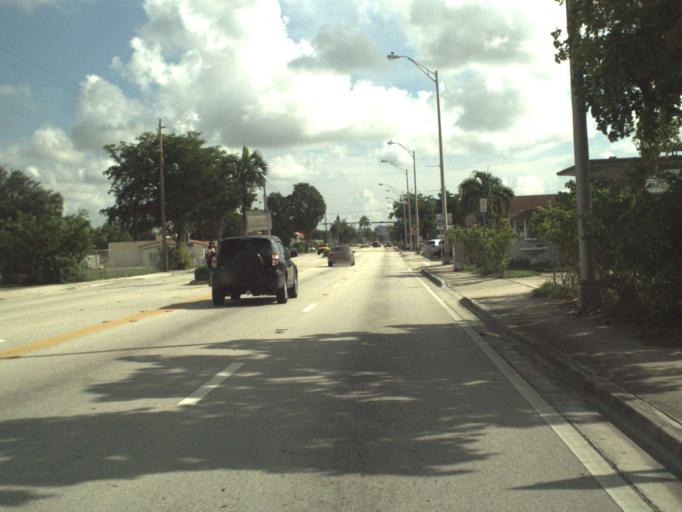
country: US
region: Florida
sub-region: Miami-Dade County
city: North Miami
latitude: 25.9045
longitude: -80.1739
